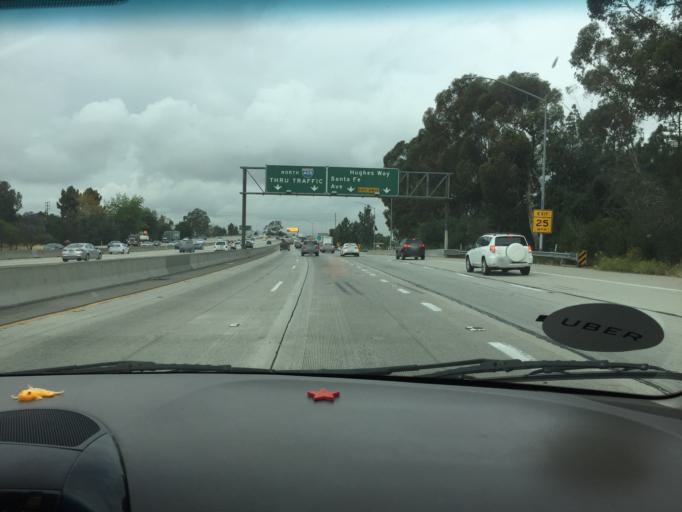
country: US
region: California
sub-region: Los Angeles County
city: Signal Hill
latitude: 33.8265
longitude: -118.2117
